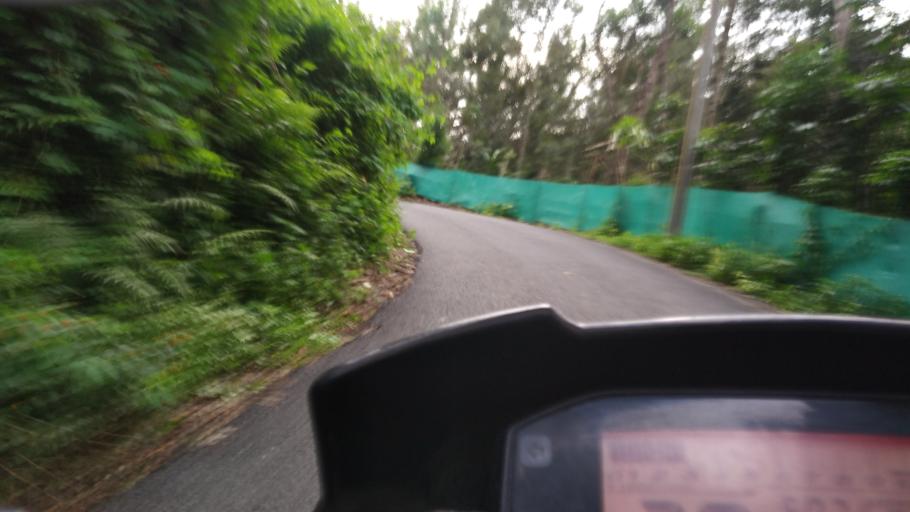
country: IN
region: Tamil Nadu
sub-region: Theni
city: Bodinayakkanur
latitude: 10.0336
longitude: 77.2300
